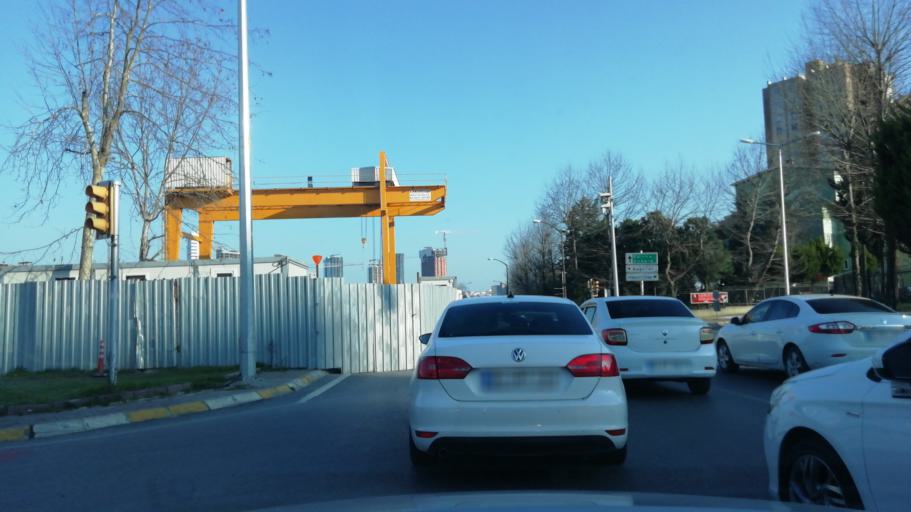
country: TR
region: Istanbul
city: Mahmutbey
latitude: 41.0477
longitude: 28.8002
